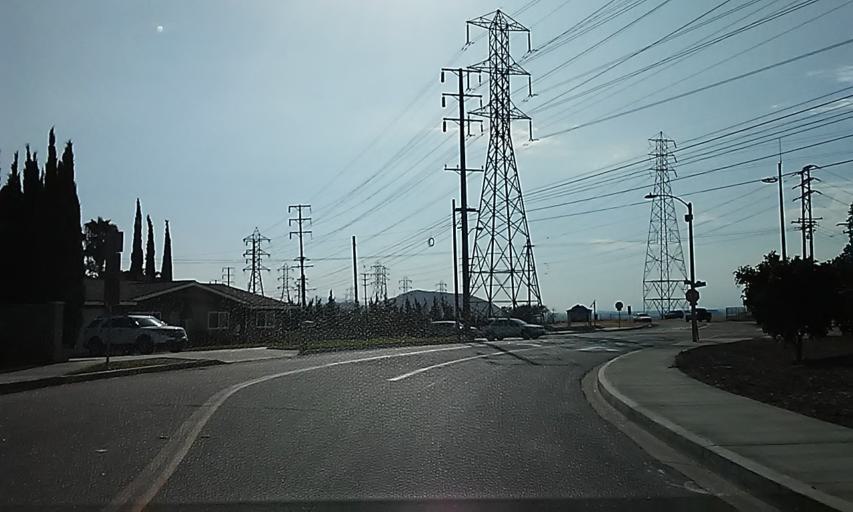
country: US
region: California
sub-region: San Bernardino County
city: Grand Terrace
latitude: 34.0418
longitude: -117.3124
